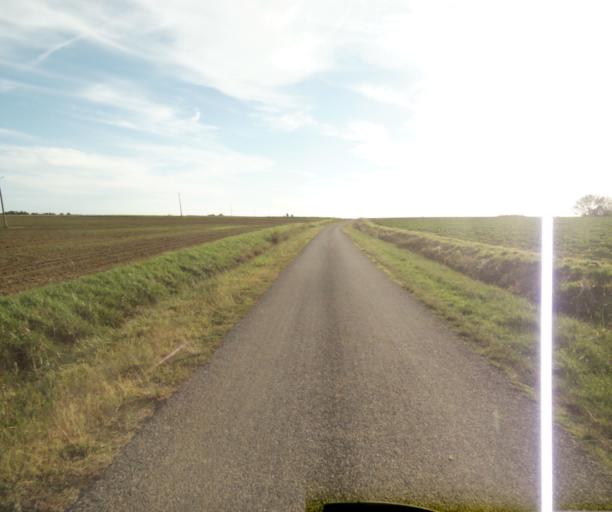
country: FR
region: Midi-Pyrenees
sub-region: Departement du Tarn-et-Garonne
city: Finhan
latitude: 43.9255
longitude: 1.1378
